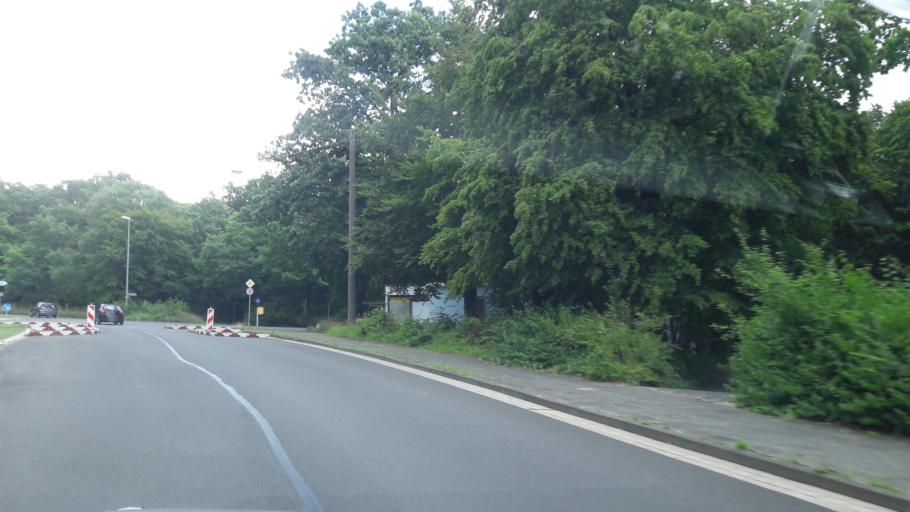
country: DE
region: Lower Saxony
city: Diekholzen
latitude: 52.1174
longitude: 9.9006
